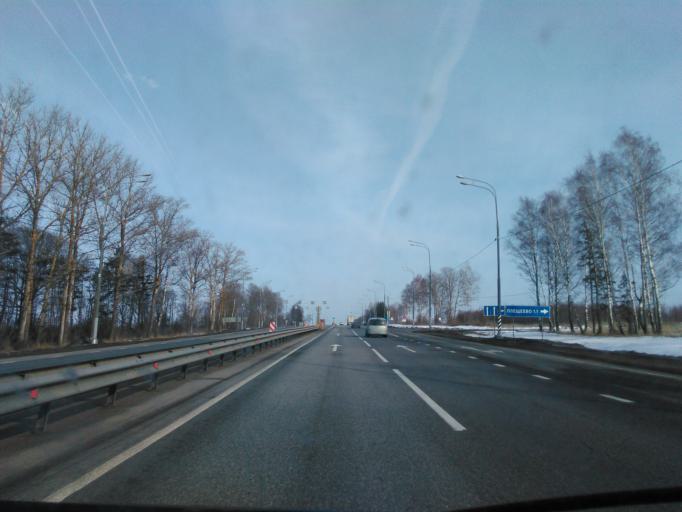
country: RU
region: Smolensk
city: Safonovo
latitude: 55.1271
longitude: 33.1405
